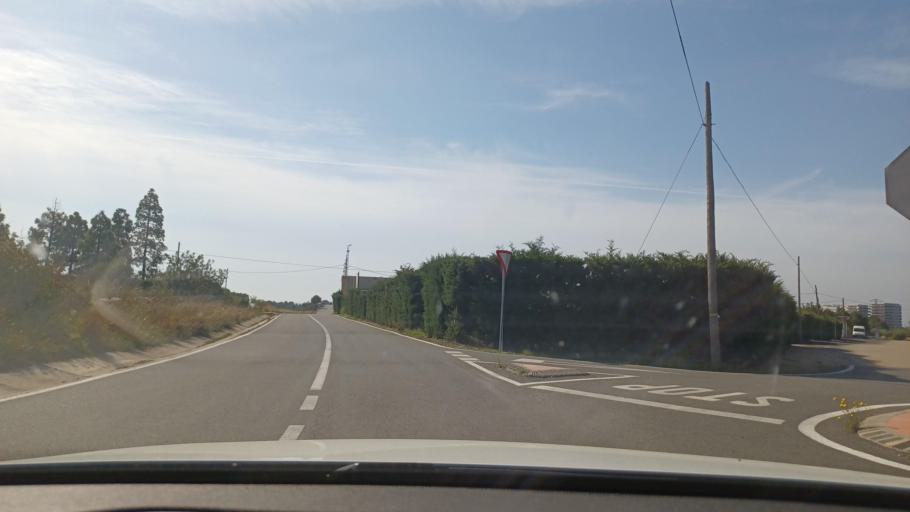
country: ES
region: Catalonia
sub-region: Provincia de Tarragona
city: L'Ampolla
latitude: 40.8217
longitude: 0.7144
